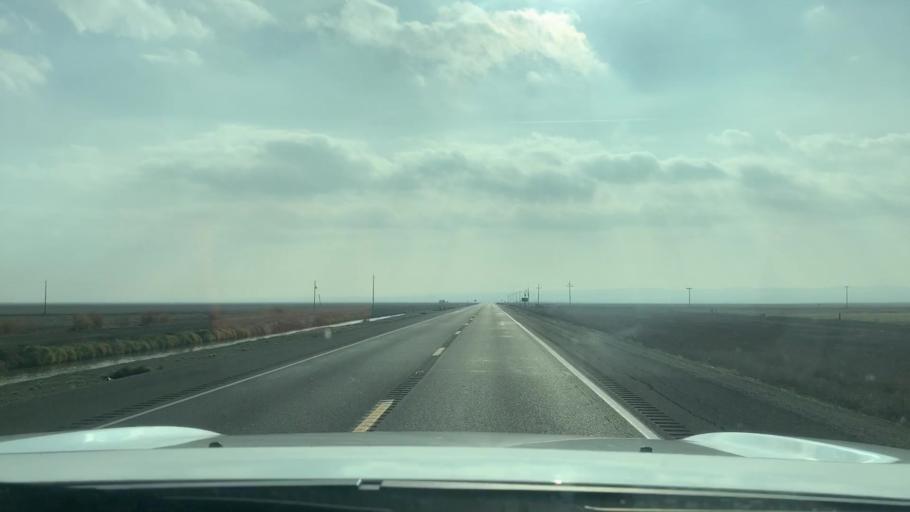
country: US
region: California
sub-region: Kings County
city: Kettleman City
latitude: 36.0967
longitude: -119.9089
